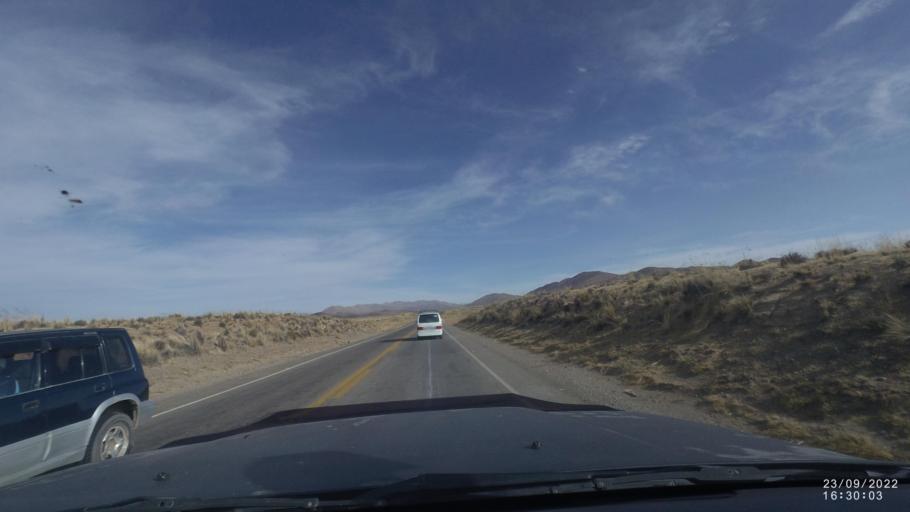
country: BO
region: Oruro
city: Machacamarca
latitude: -18.1499
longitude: -66.9890
